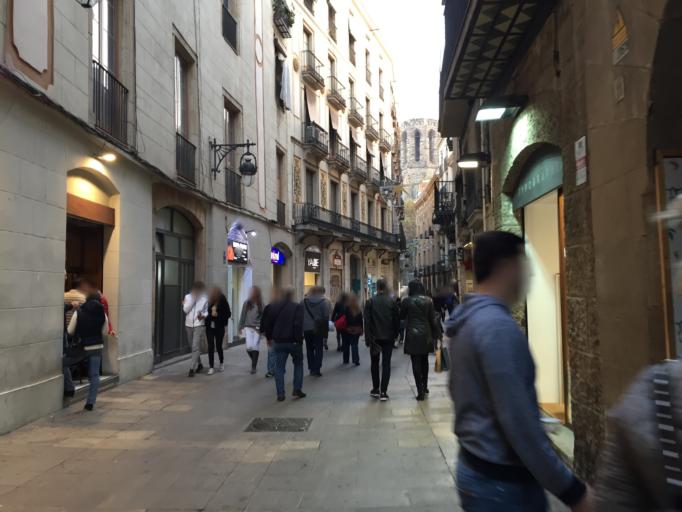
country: ES
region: Catalonia
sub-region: Provincia de Barcelona
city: Ciutat Vella
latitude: 41.3836
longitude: 2.1739
